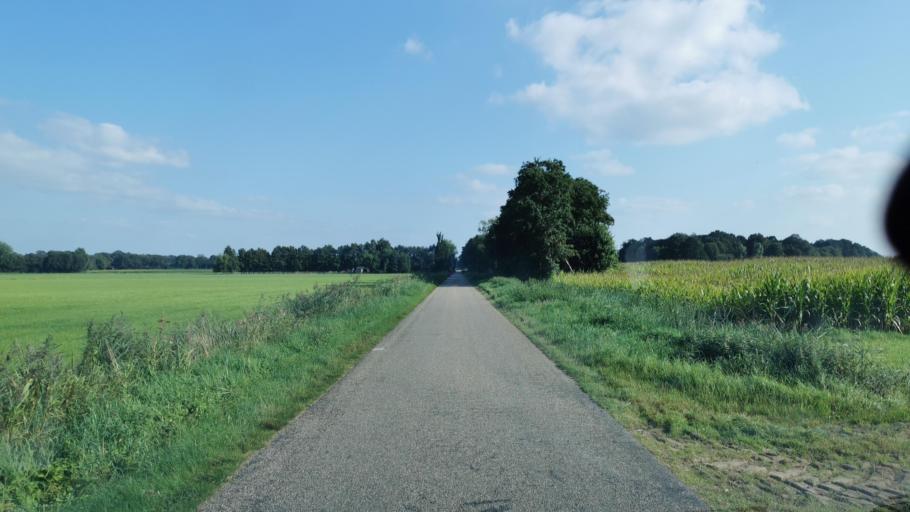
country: NL
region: Overijssel
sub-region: Gemeente Borne
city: Borne
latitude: 52.3327
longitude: 6.7670
